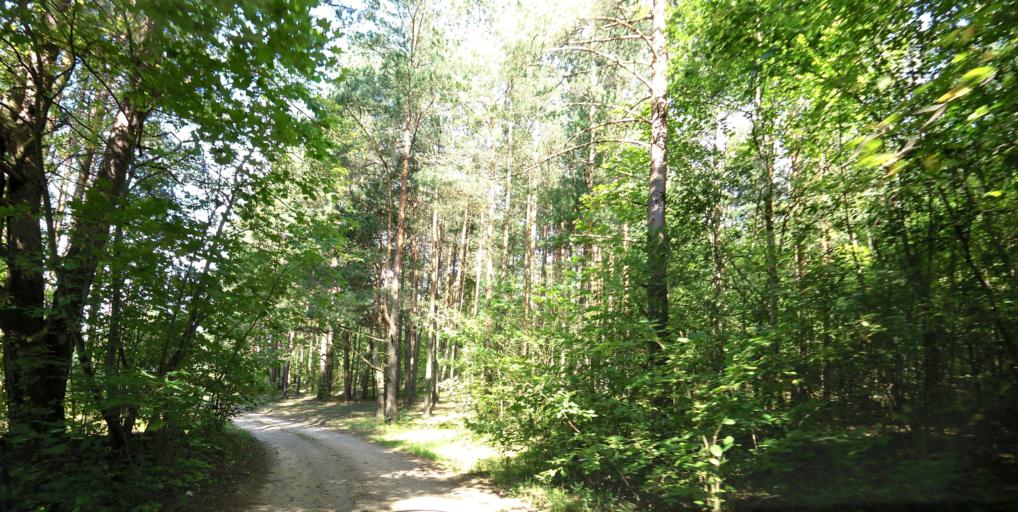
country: LT
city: Grigiskes
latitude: 54.7343
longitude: 25.0425
